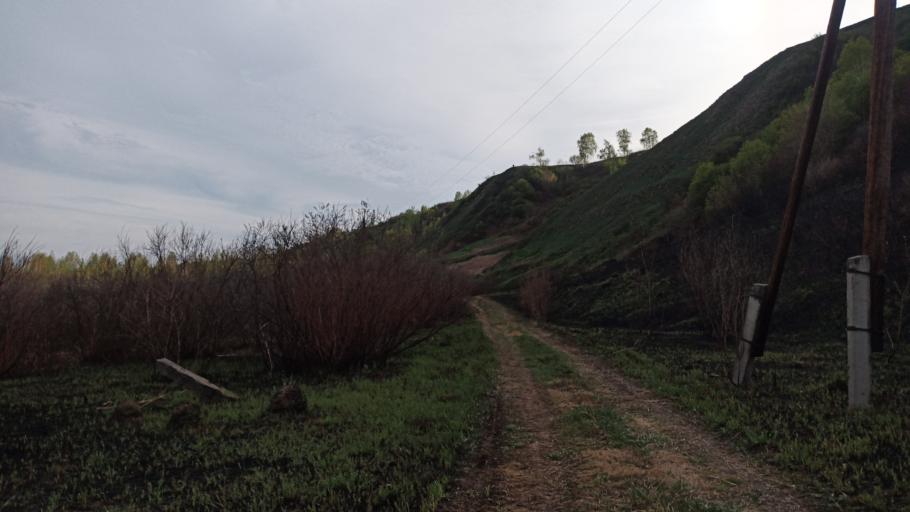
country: RU
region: Altai Krai
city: Yuzhnyy
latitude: 53.2209
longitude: 83.7235
